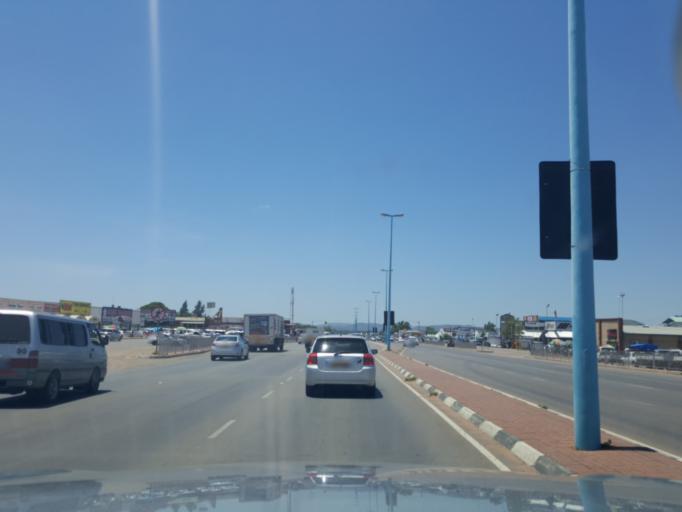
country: BW
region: Kweneng
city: Mogoditshane
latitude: -24.6200
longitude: 25.8661
